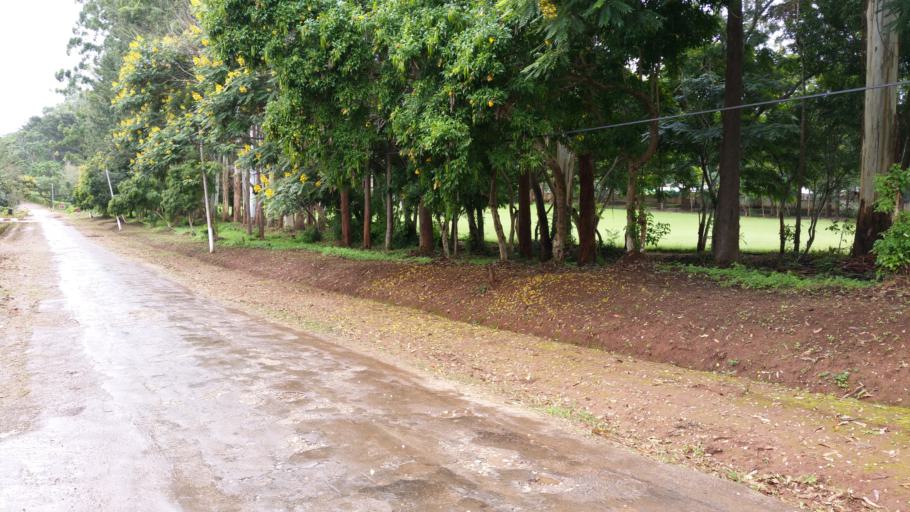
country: MM
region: Mandalay
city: Yamethin
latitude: 20.6230
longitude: 96.5551
